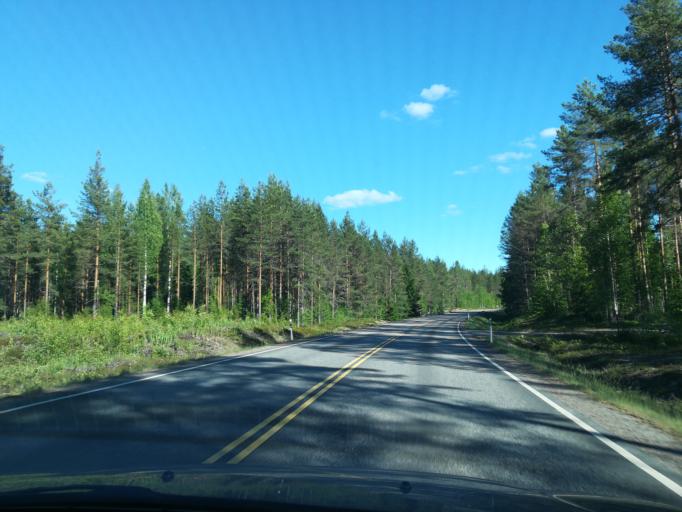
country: FI
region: South Karelia
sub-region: Imatra
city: Ruokolahti
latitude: 61.3983
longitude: 28.6305
